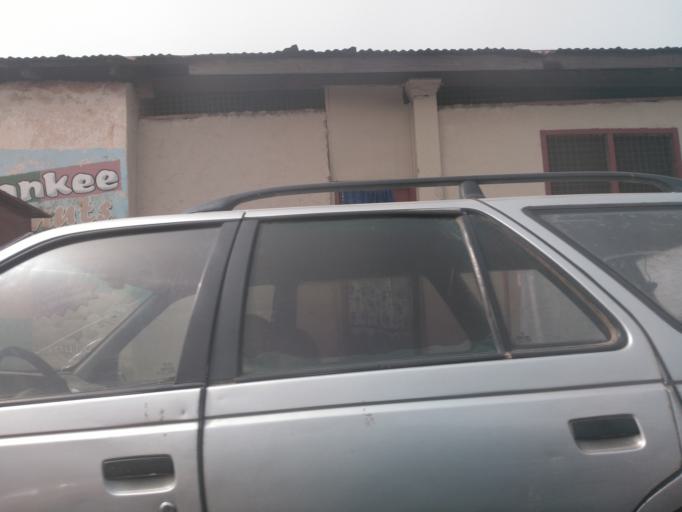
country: GH
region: Ashanti
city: Kumasi
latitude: 6.7045
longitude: -1.6230
